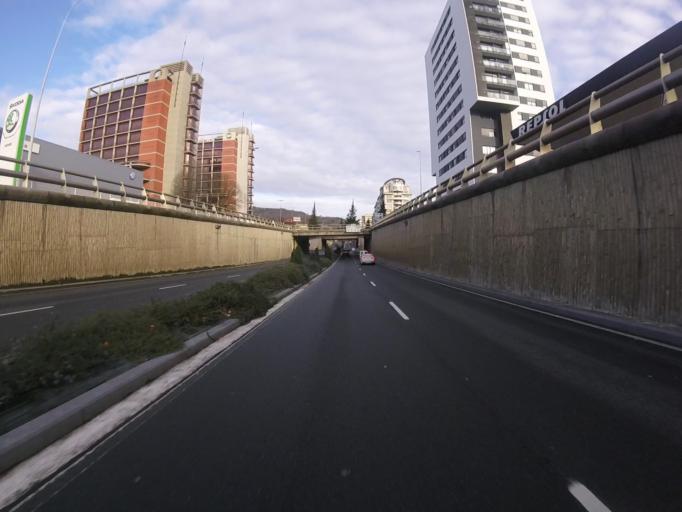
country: ES
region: Basque Country
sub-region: Provincia de Guipuzcoa
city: San Sebastian
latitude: 43.3007
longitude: -2.0023
